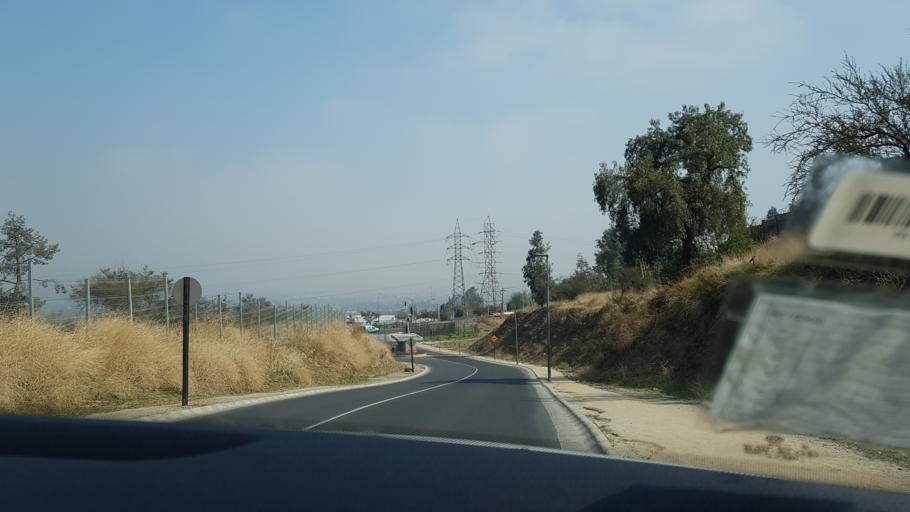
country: CL
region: Santiago Metropolitan
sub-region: Provincia de Santiago
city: Villa Presidente Frei, Nunoa, Santiago, Chile
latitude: -33.4800
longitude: -70.5221
